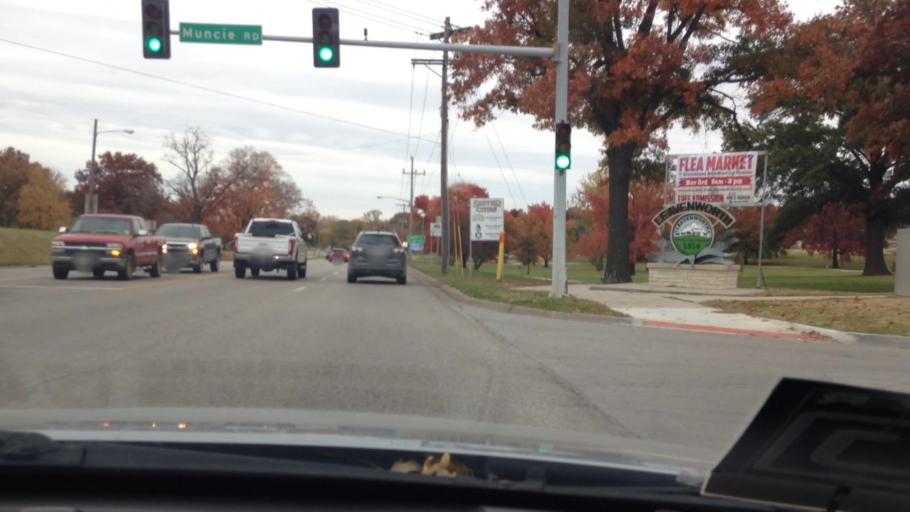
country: US
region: Kansas
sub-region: Leavenworth County
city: Lansing
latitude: 39.2742
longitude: -94.8997
